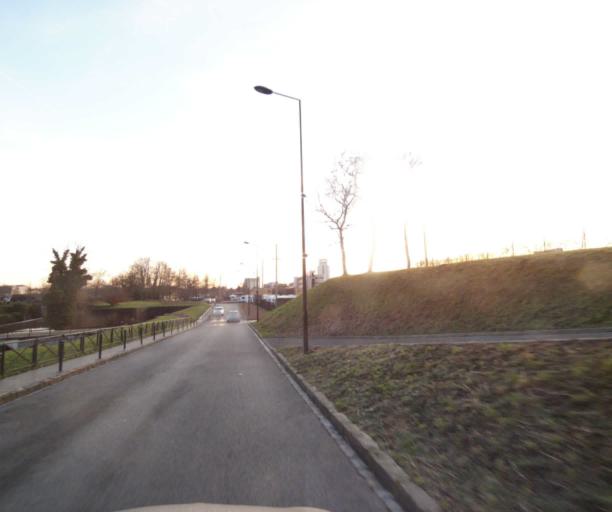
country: FR
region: Nord-Pas-de-Calais
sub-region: Departement du Nord
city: Anzin
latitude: 50.3583
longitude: 3.5146
